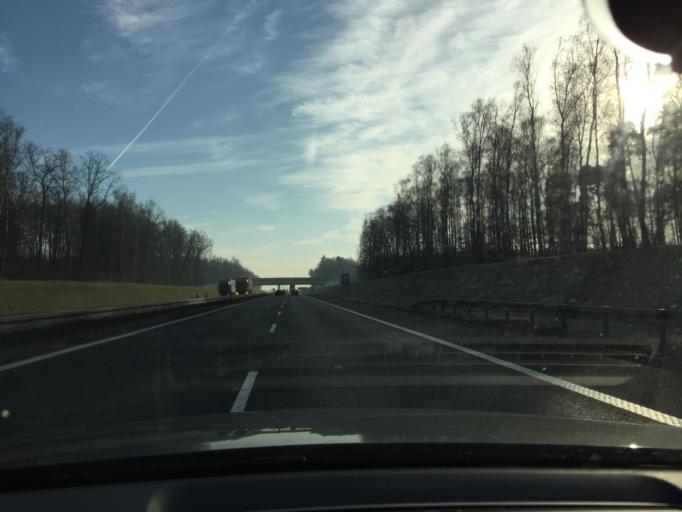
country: PL
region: Silesian Voivodeship
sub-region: Powiat gliwicki
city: Sosnicowice
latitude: 50.2897
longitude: 18.5635
